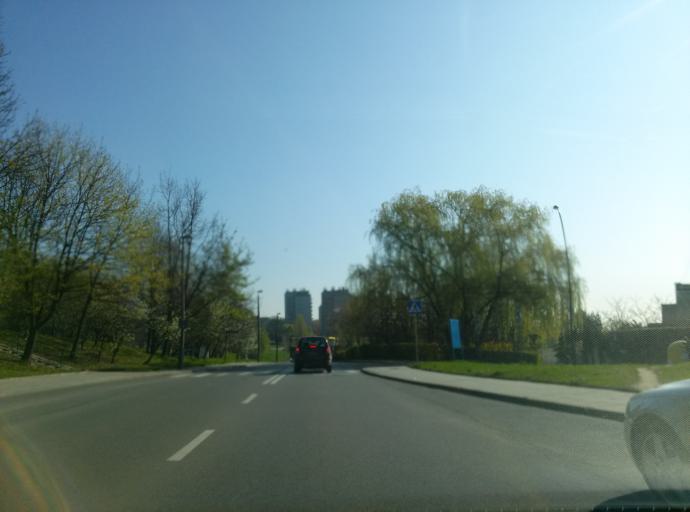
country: PL
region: Lesser Poland Voivodeship
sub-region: Powiat wielicki
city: Kokotow
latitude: 50.0948
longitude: 20.0466
